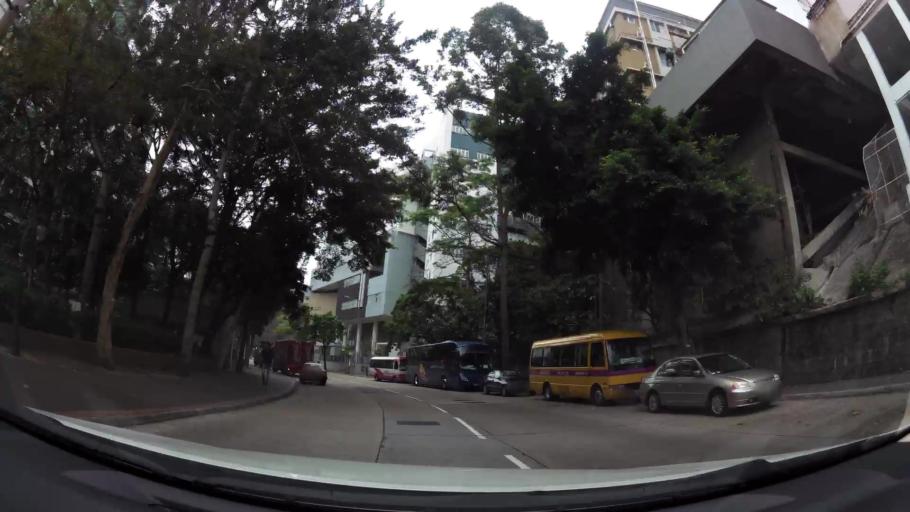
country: HK
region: Sham Shui Po
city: Sham Shui Po
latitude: 22.3301
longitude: 114.1720
